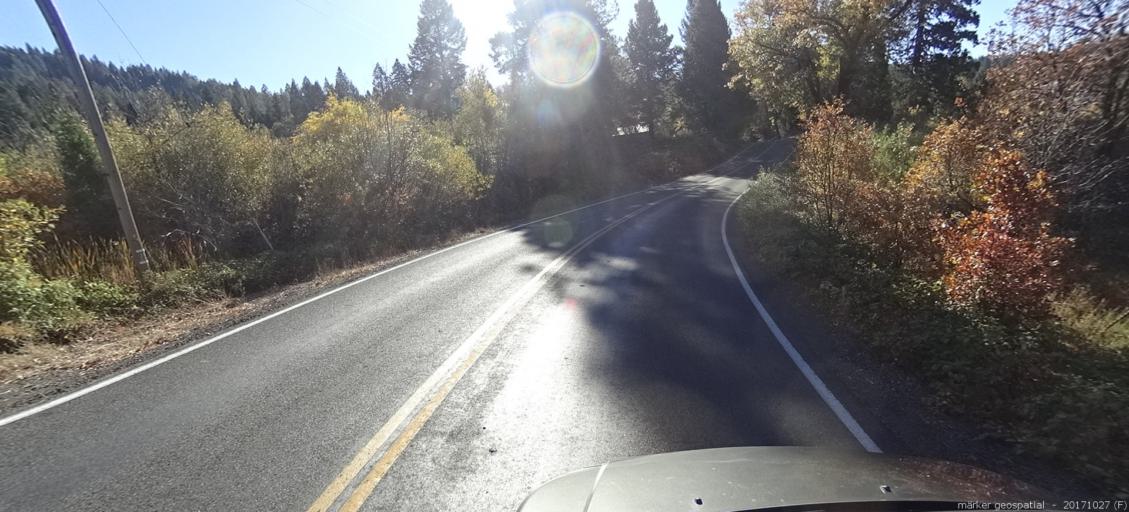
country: US
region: California
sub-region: Shasta County
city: Burney
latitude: 40.9080
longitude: -121.9048
